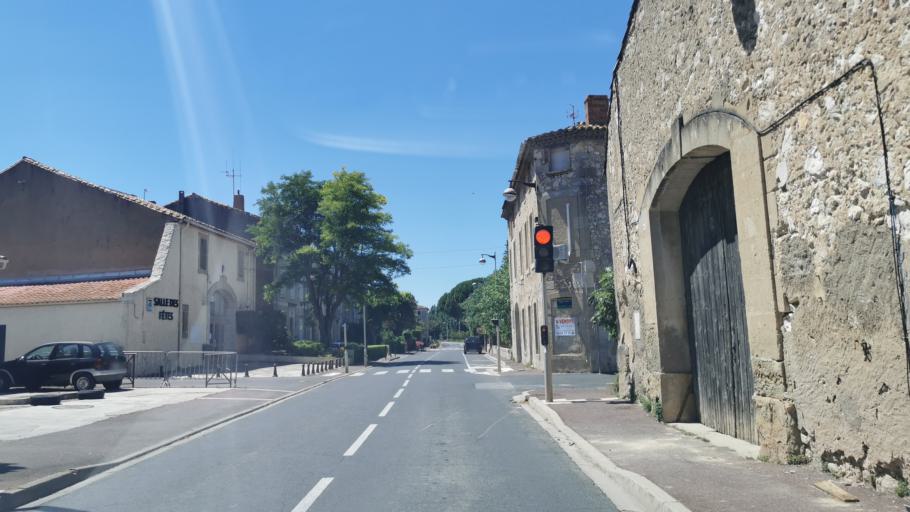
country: FR
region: Languedoc-Roussillon
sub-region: Departement de l'Aude
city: Fleury
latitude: 43.2297
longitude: 3.1316
